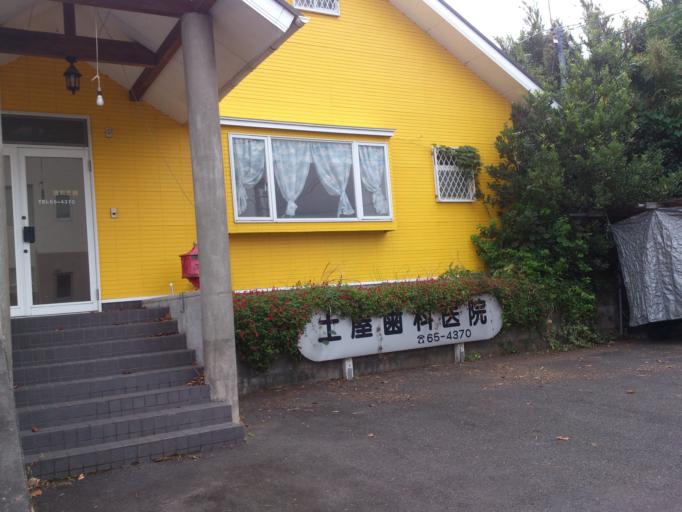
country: JP
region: Kagoshima
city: Kanoya
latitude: 31.3491
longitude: 130.9481
